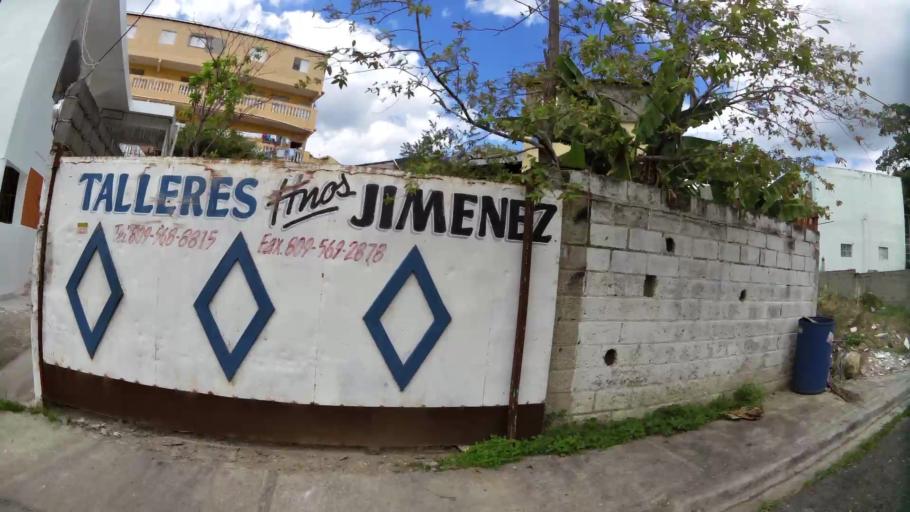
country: DO
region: Nacional
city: Ensanche Luperon
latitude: 18.5280
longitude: -69.9033
